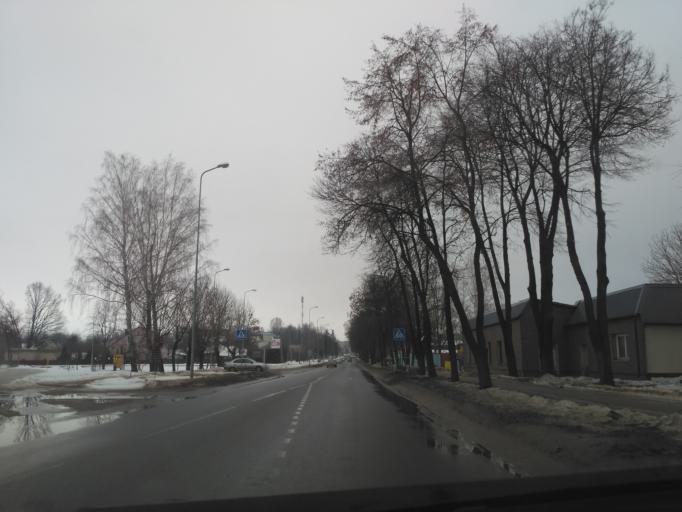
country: BY
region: Minsk
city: Horad Zhodzina
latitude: 54.0966
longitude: 28.3378
